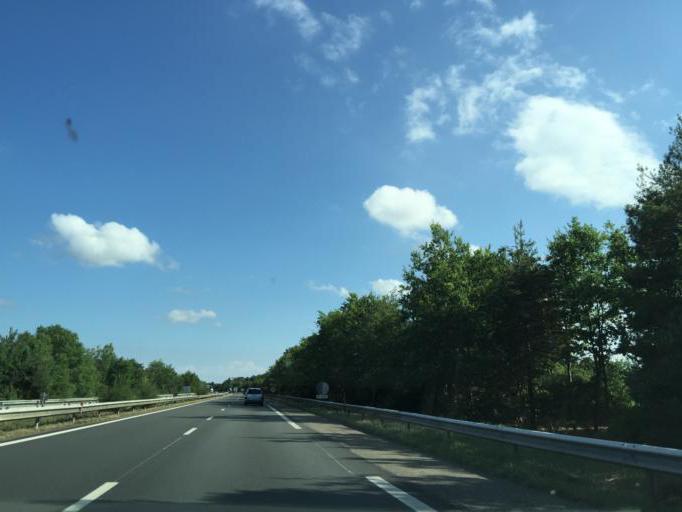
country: FR
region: Rhone-Alpes
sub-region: Departement de la Loire
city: Balbigny
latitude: 45.8126
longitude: 4.1177
